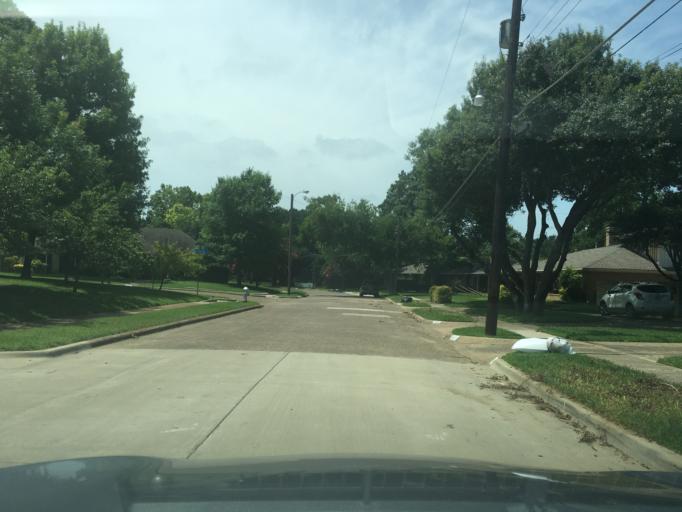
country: US
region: Texas
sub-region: Dallas County
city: Richardson
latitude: 32.9470
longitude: -96.7537
